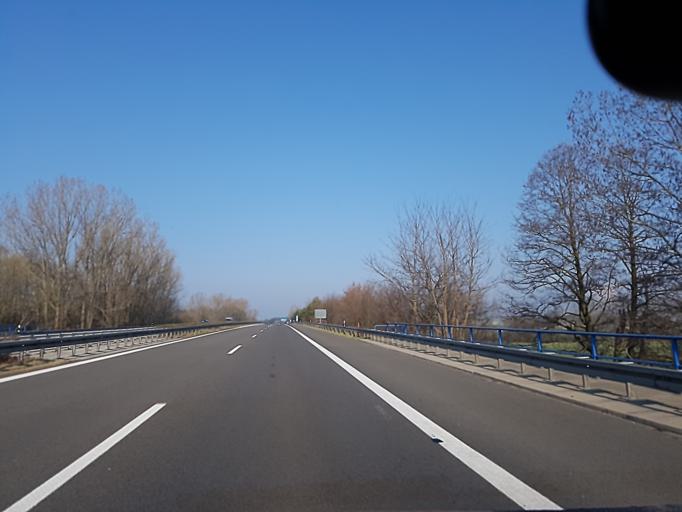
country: DE
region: Brandenburg
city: Forst
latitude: 51.7099
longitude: 14.6191
